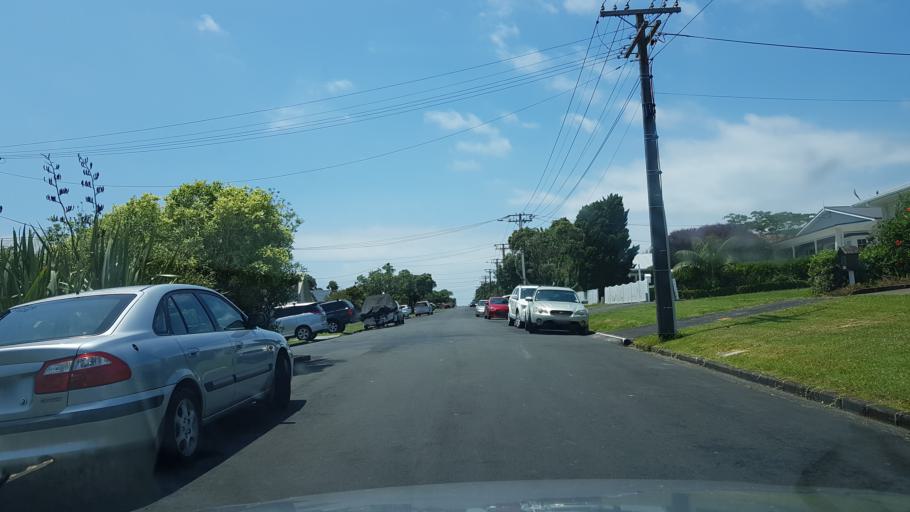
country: NZ
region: Auckland
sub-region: Auckland
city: North Shore
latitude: -36.8170
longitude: 174.7858
